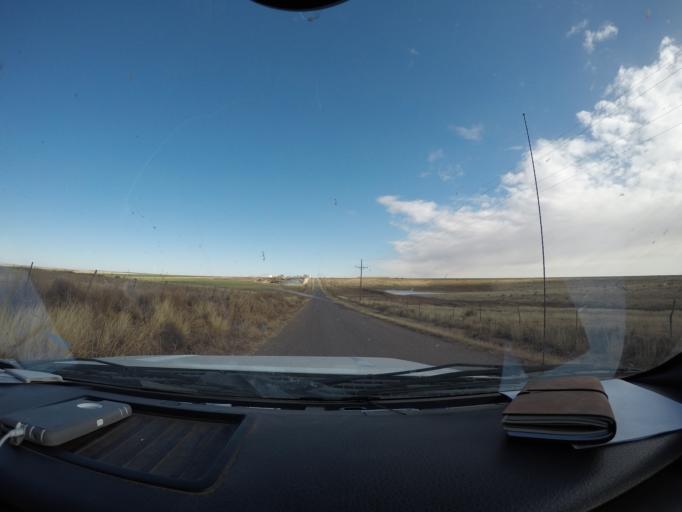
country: US
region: Texas
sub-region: Parmer County
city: Bovina
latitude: 34.6325
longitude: -103.0889
